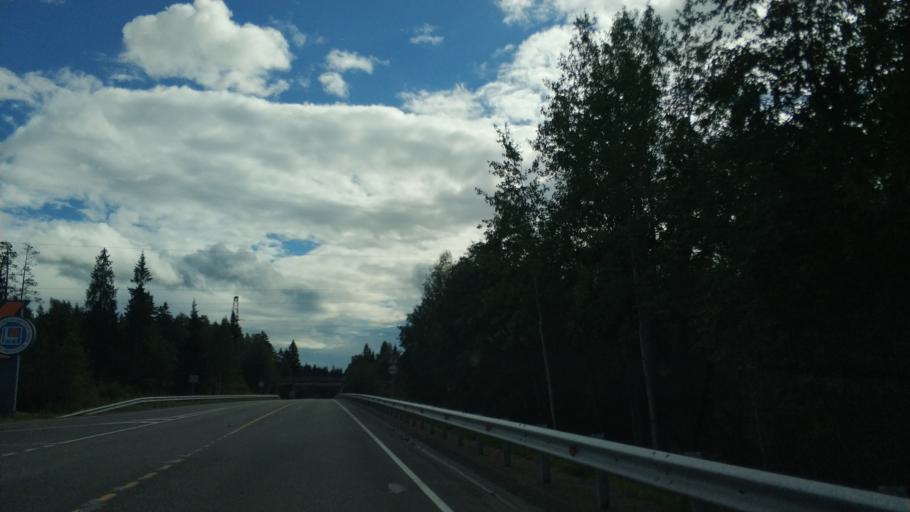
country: RU
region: Republic of Karelia
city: Khelyulya
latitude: 61.7808
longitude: 30.6582
